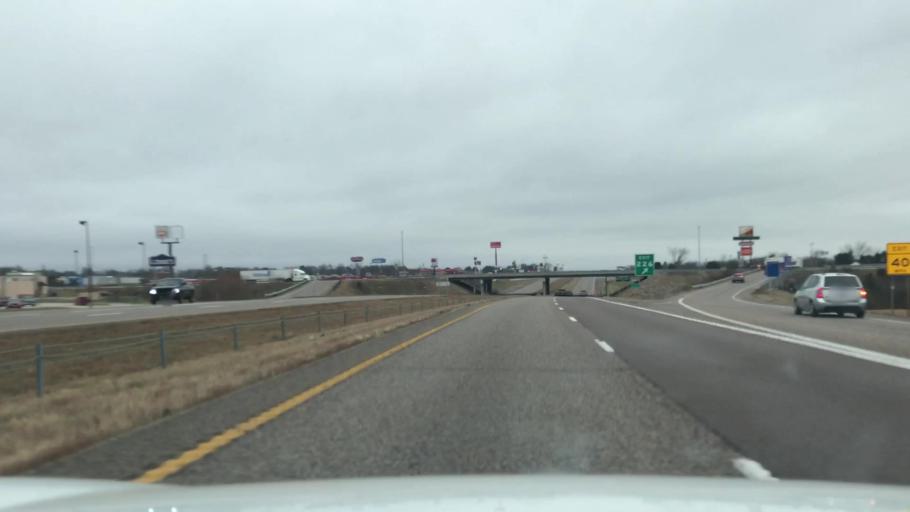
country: US
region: Missouri
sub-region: Franklin County
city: Sullivan
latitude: 38.2265
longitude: -91.1536
